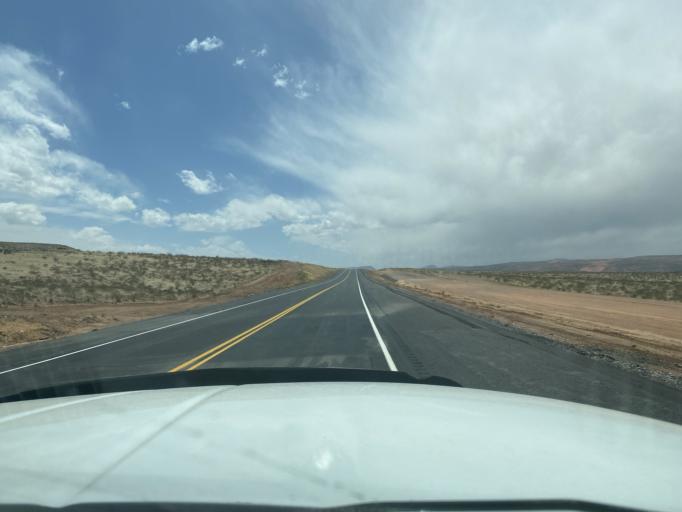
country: US
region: Utah
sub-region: Washington County
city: Hurricane
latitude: 37.1628
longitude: -113.3459
